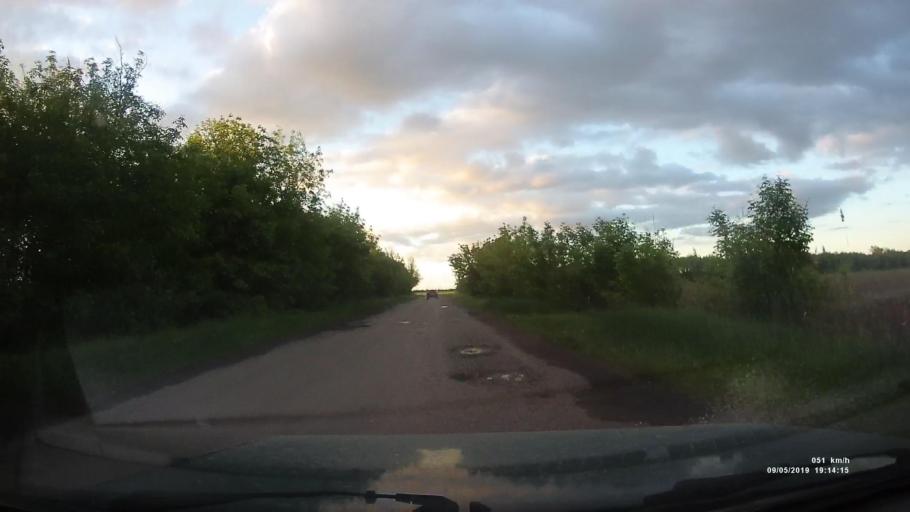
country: RU
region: Krasnodarskiy
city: Kanelovskaya
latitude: 46.7567
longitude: 39.2140
